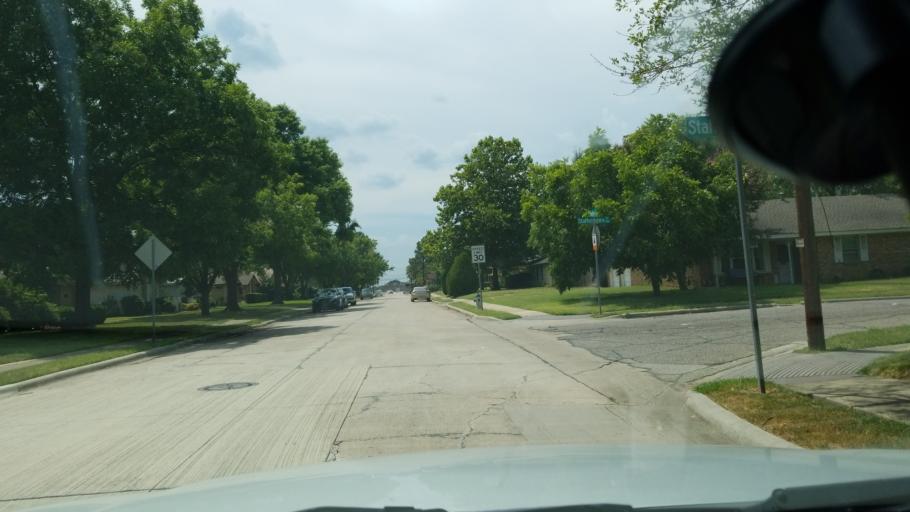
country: US
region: Texas
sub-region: Dallas County
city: Irving
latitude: 32.8188
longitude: -96.9861
